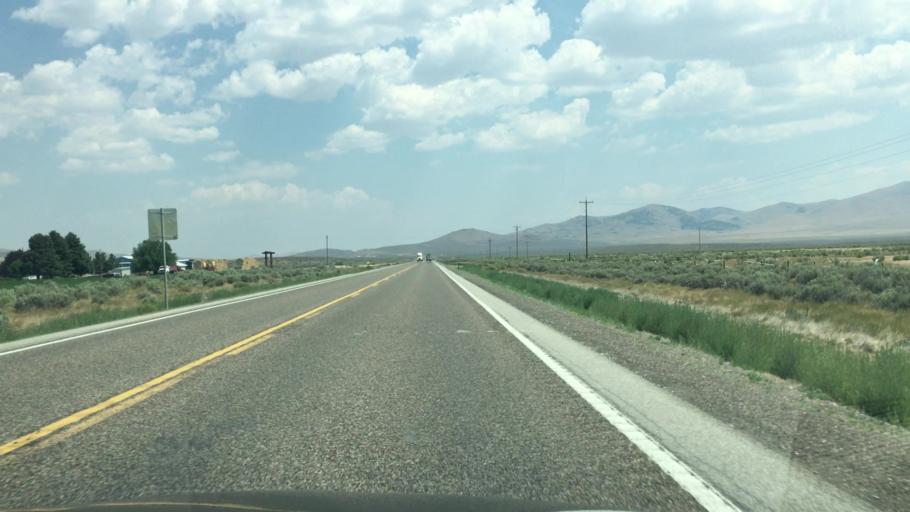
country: US
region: Nevada
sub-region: Elko County
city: Wells
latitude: 41.1425
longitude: -114.9113
